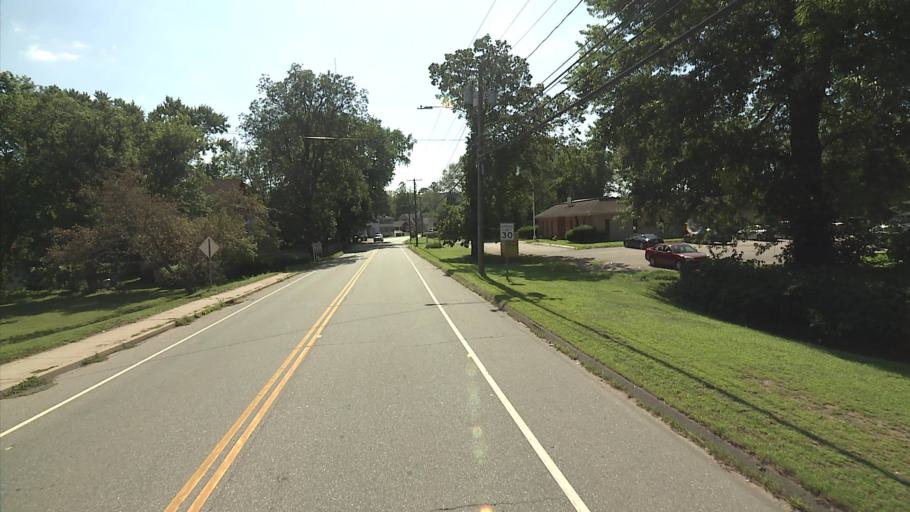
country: US
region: Connecticut
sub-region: Windham County
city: Willimantic
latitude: 41.7159
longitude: -72.1931
